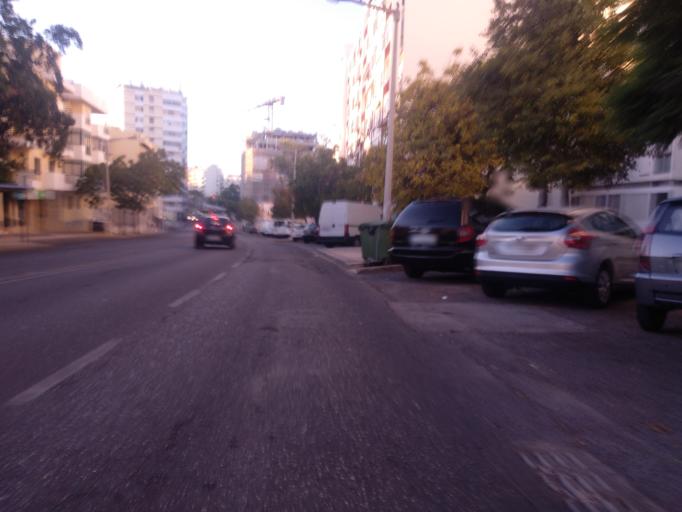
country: PT
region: Faro
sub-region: Faro
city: Faro
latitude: 37.0224
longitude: -7.9248
